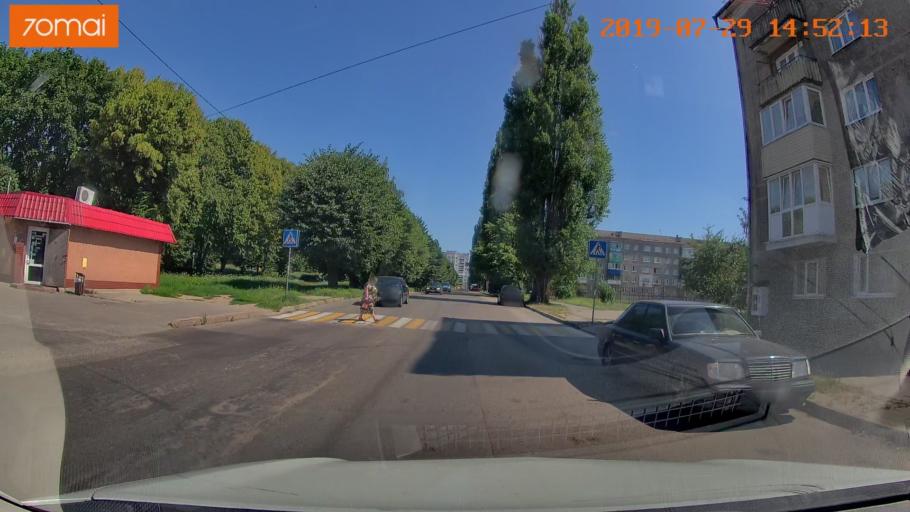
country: RU
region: Kaliningrad
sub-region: Gorod Kaliningrad
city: Baltiysk
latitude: 54.6624
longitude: 19.9098
